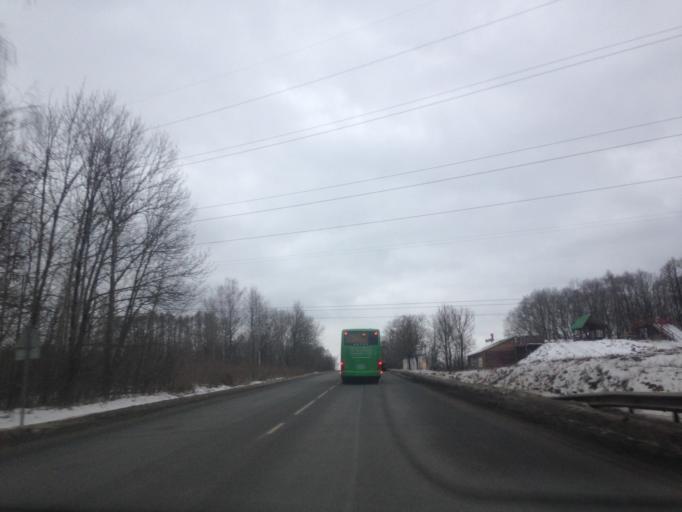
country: RU
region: Tula
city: Mendeleyevskiy
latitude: 54.1237
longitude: 37.5730
